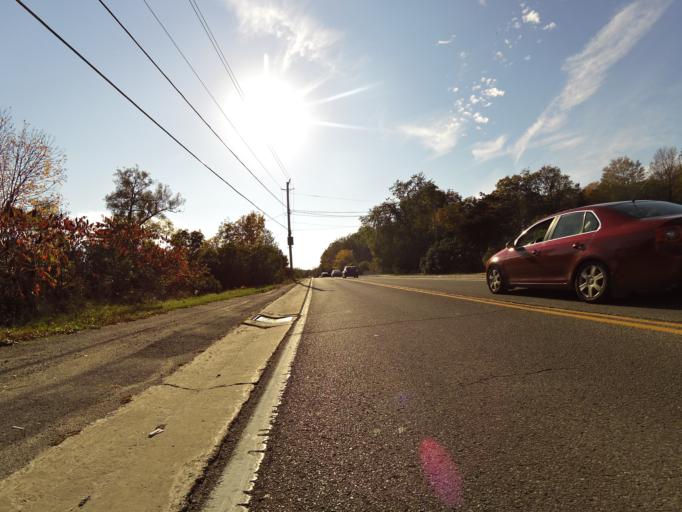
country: CA
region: Ontario
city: Kingston
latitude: 44.2384
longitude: -76.6164
